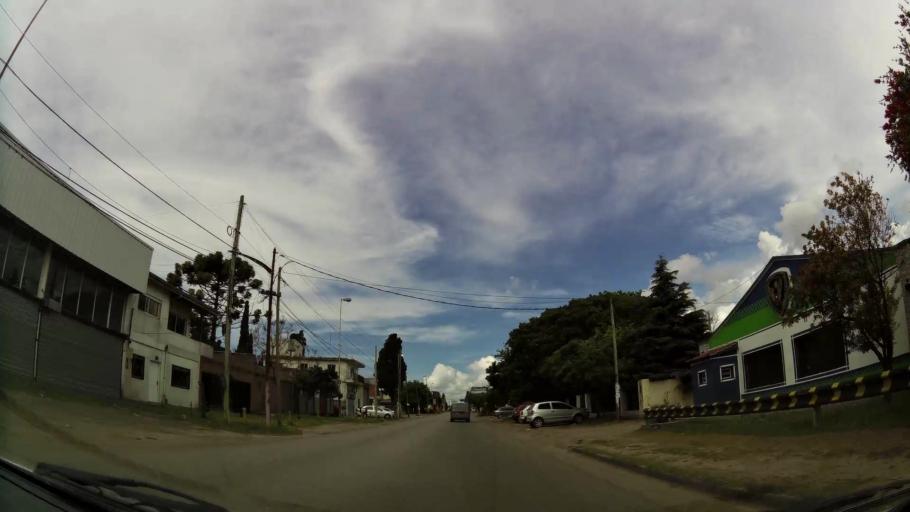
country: AR
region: Buenos Aires
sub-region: Partido de Quilmes
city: Quilmes
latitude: -34.7705
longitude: -58.2817
